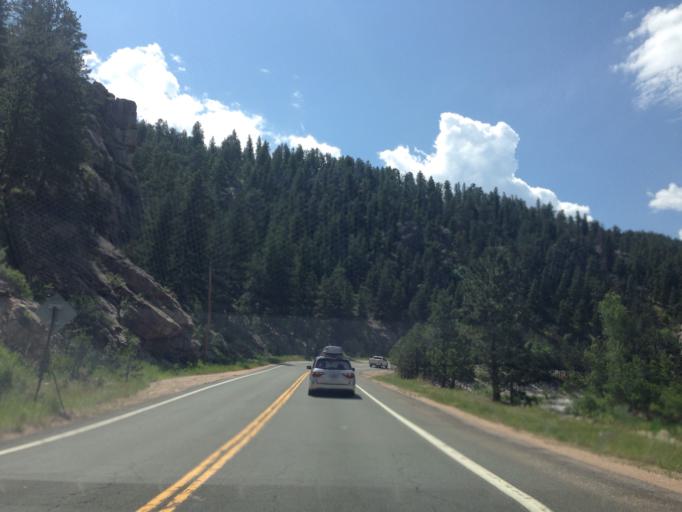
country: US
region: Colorado
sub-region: Larimer County
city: Estes Park
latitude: 40.4083
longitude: -105.4134
